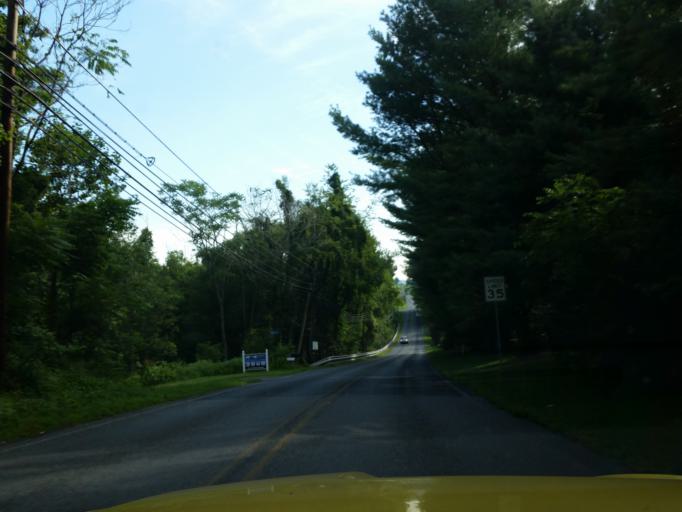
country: US
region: Pennsylvania
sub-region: Lebanon County
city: Jonestown
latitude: 40.4202
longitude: -76.4681
